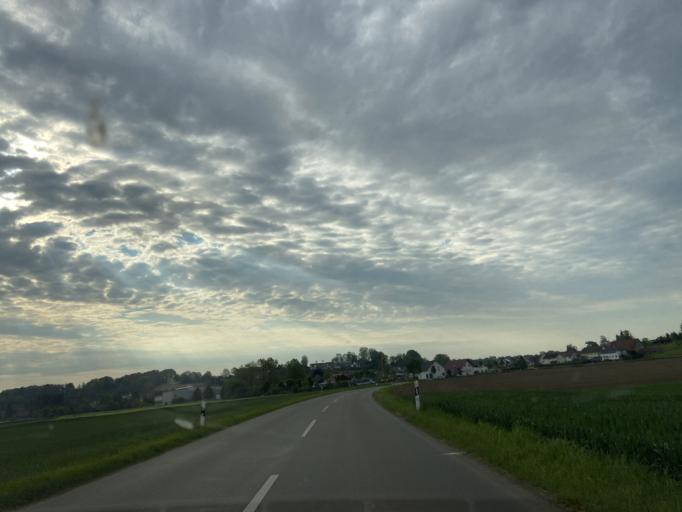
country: DE
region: Baden-Wuerttemberg
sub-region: Tuebingen Region
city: Hohentengen
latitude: 48.0386
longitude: 9.3814
